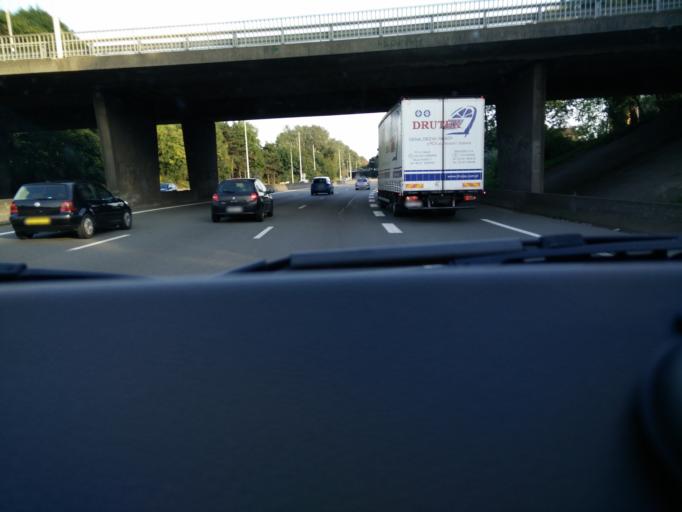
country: FR
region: Nord-Pas-de-Calais
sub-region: Departement du Nord
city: Loos
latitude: 50.6212
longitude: 3.0273
